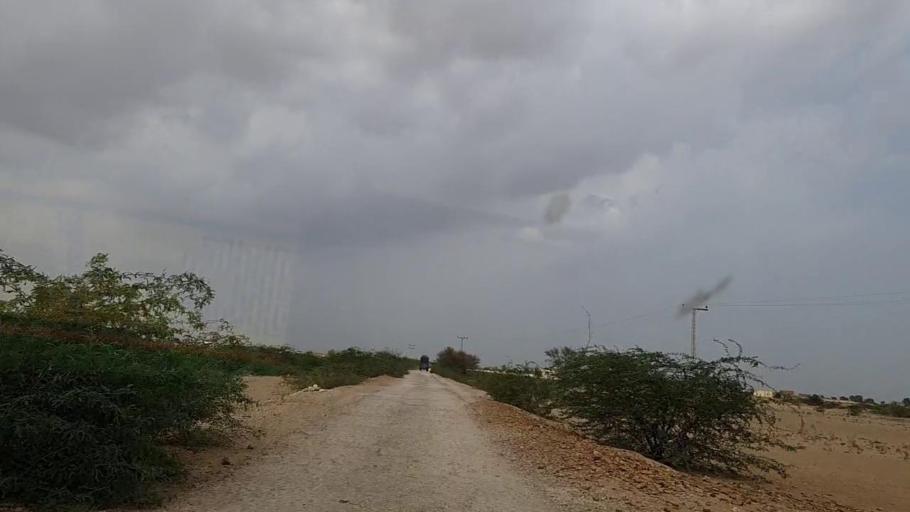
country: PK
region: Sindh
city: Kotri
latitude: 25.2864
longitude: 68.2121
